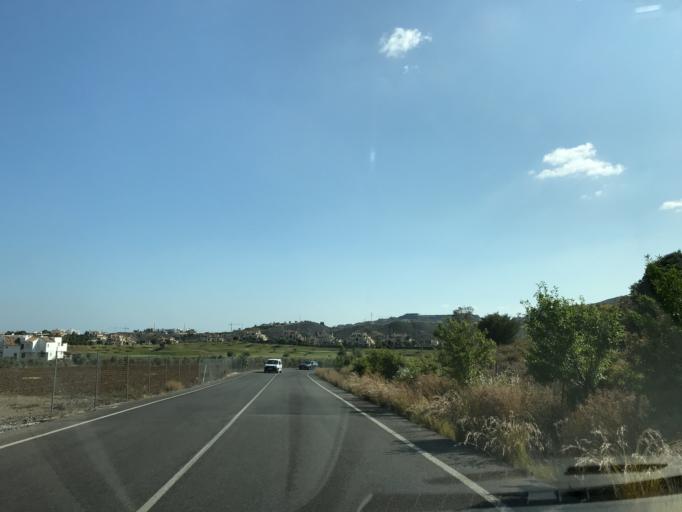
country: ES
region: Andalusia
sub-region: Provincia de Malaga
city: Benahavis
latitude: 36.5075
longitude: -5.0186
